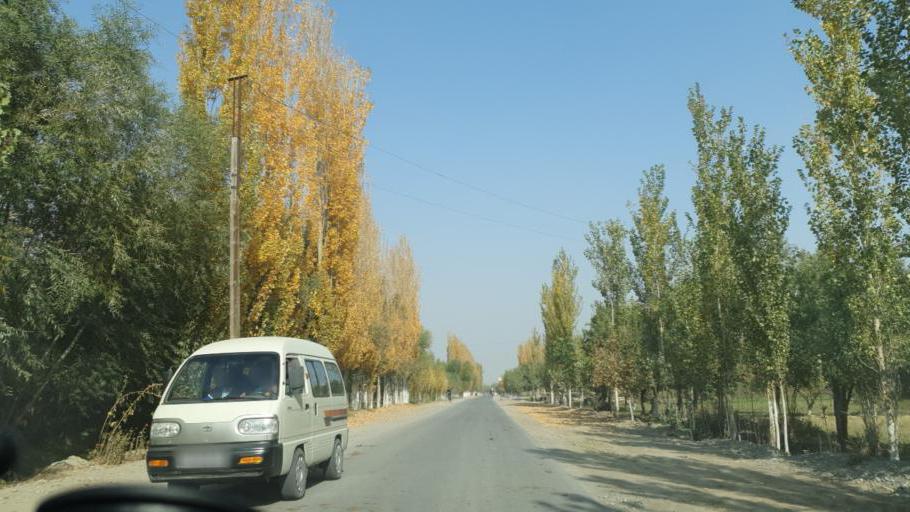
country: UZ
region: Fergana
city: Beshariq
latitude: 40.4893
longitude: 70.6205
